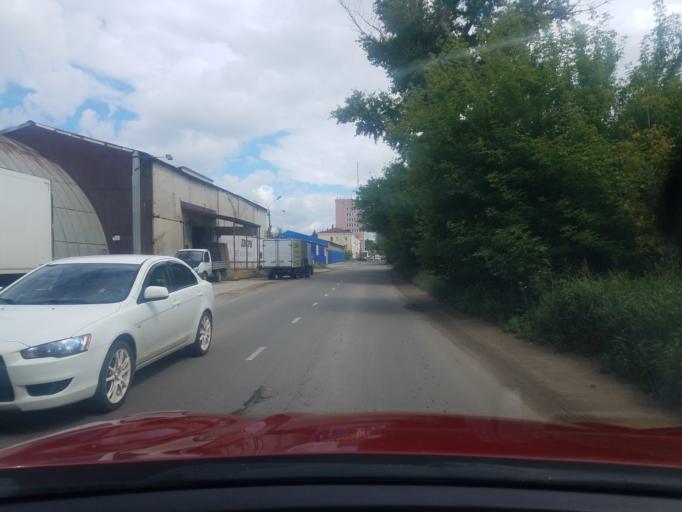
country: RU
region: Orjol
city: Znamenka
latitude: 52.9184
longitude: 35.9883
